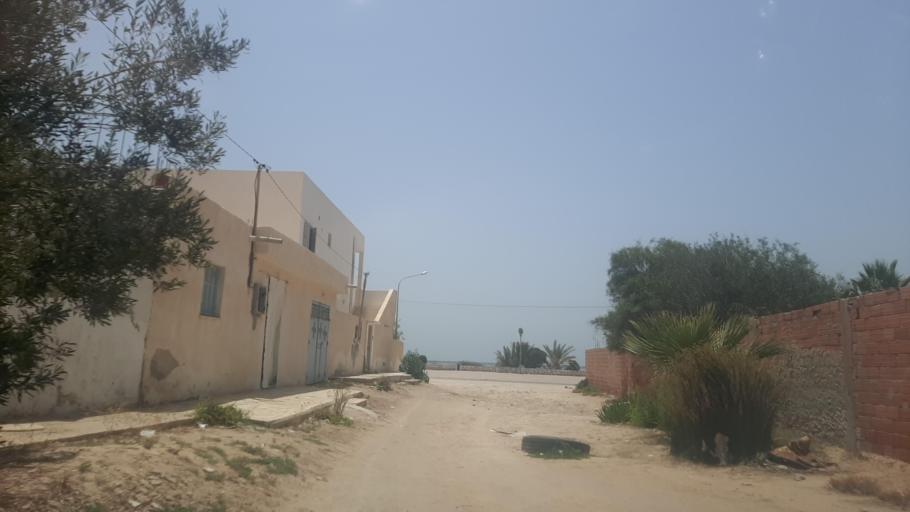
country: TN
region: Safaqis
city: Al Qarmadah
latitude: 34.7034
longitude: 11.2032
